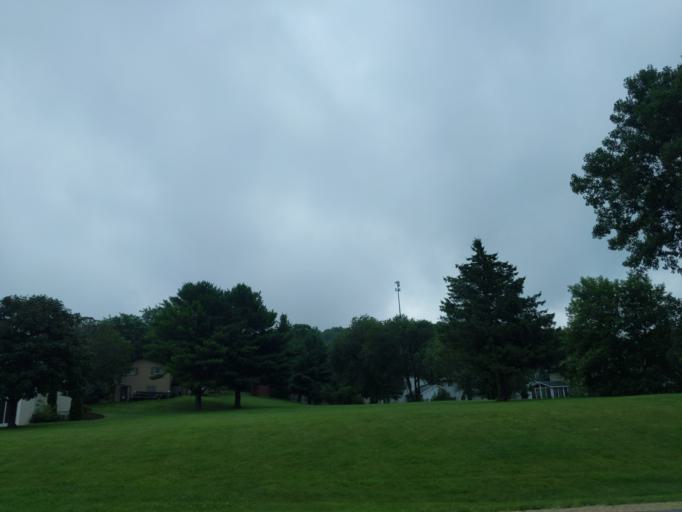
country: US
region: Wisconsin
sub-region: Dane County
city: Black Earth
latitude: 43.1283
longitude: -89.7491
